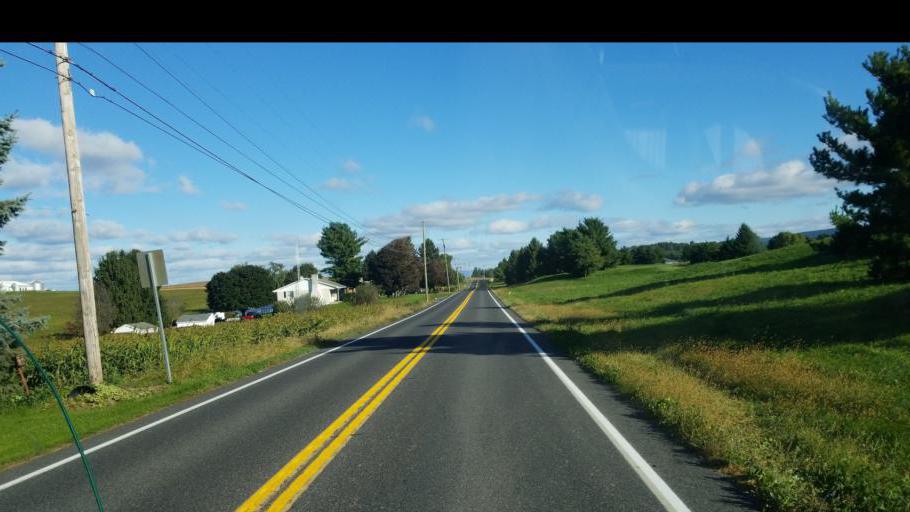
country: US
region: Pennsylvania
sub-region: Franklin County
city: Mont Alto
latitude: 39.8565
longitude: -77.5603
